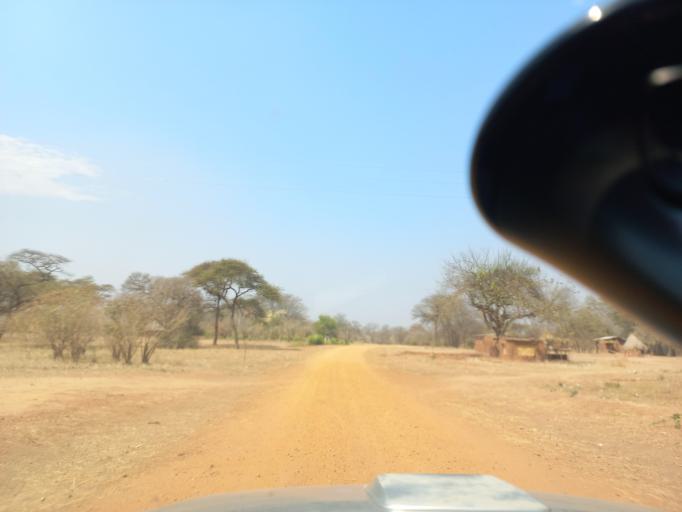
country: ZW
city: Chirundu
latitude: -15.9470
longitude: 28.8112
